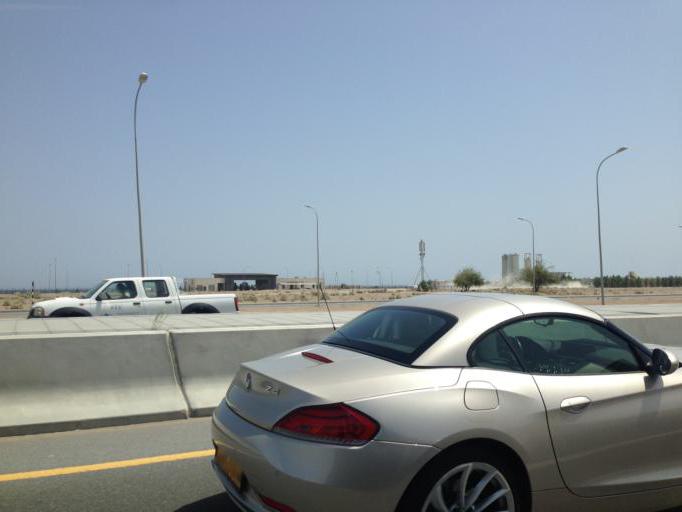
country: OM
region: Muhafazat Masqat
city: Bawshar
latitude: 23.6059
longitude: 58.3219
